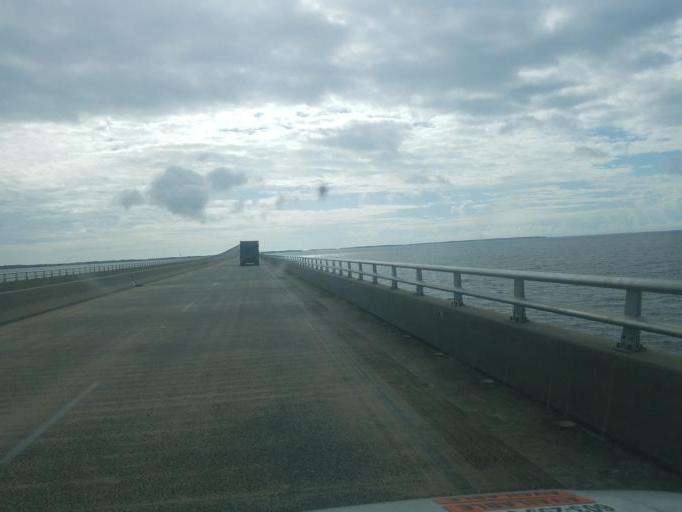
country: US
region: North Carolina
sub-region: Dare County
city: Manteo
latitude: 35.8863
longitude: -75.7282
